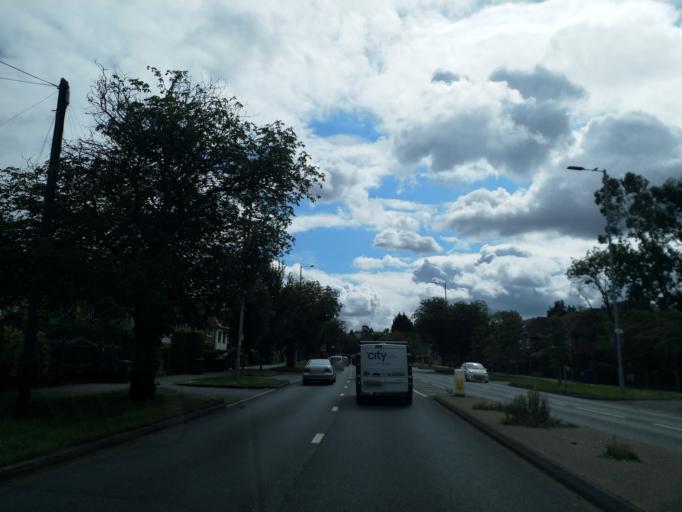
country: GB
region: England
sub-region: Greater London
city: Belsize Park
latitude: 51.5835
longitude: -0.1670
